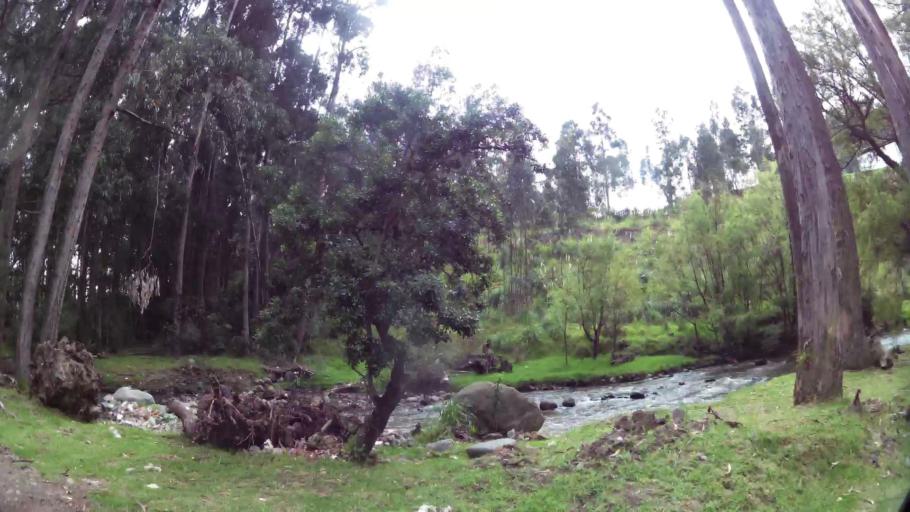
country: EC
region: Azuay
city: Cuenca
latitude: -2.9181
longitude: -79.0132
